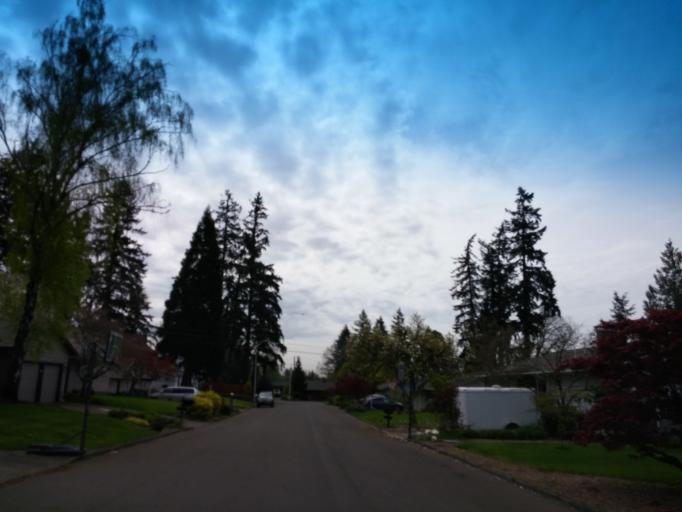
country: US
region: Oregon
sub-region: Washington County
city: Cedar Mill
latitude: 45.5299
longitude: -122.8109
